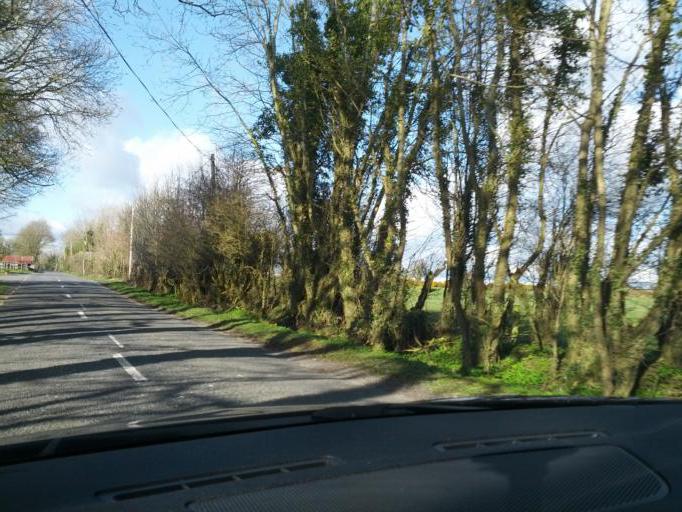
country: IE
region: Connaught
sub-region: Roscommon
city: Castlerea
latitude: 53.5389
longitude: -8.5542
